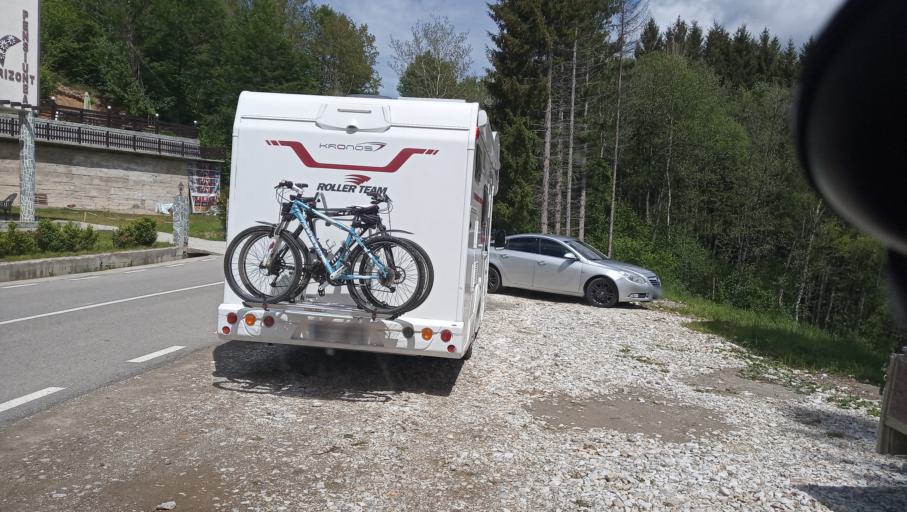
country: RO
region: Caras-Severin
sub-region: Comuna Brebu Nou
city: Brebu Nou
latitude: 45.2186
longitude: 22.1414
